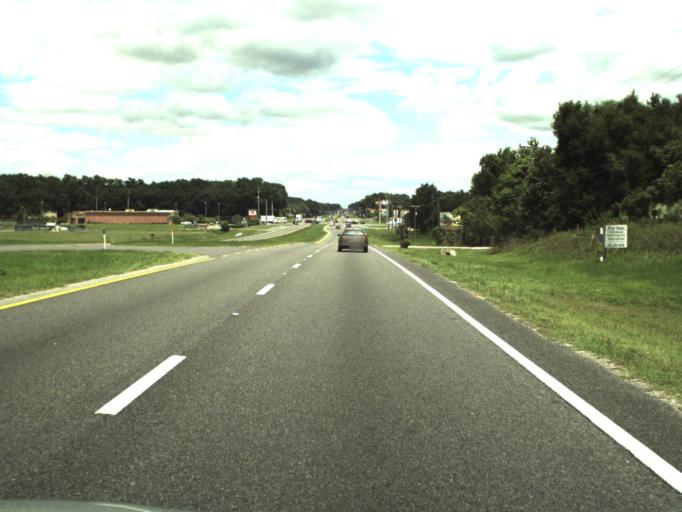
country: US
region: Florida
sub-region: Marion County
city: Ocala
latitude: 29.2551
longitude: -82.1520
